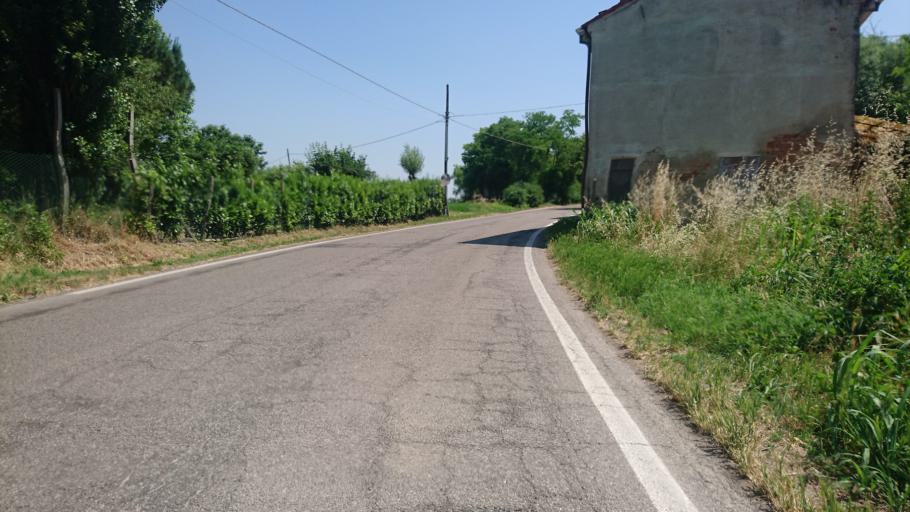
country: IT
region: Veneto
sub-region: Provincia di Padova
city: Granze
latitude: 45.1646
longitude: 11.7311
